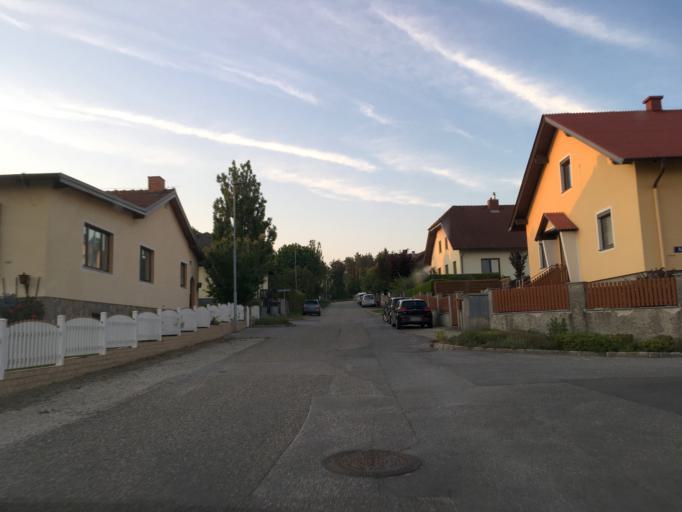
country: AT
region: Lower Austria
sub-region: Politischer Bezirk Korneuburg
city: Stockerau
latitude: 48.3916
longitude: 16.1952
